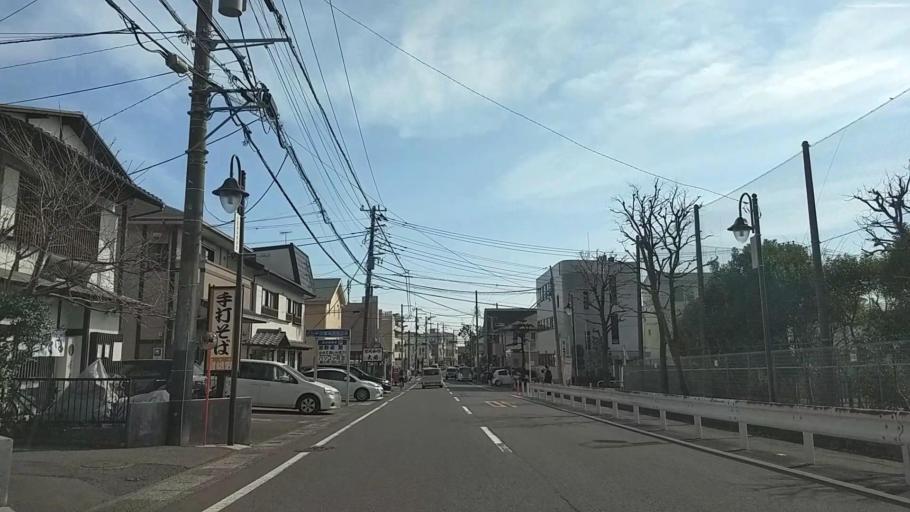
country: JP
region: Kanagawa
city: Fujisawa
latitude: 35.3250
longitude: 139.4536
